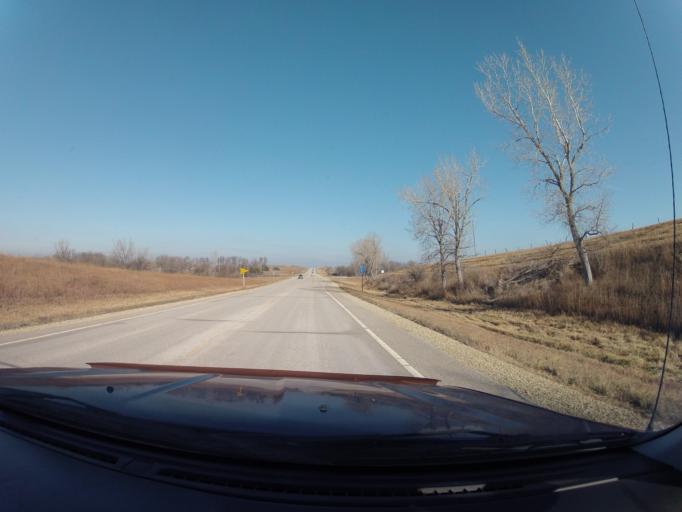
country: US
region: Kansas
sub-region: Marshall County
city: Blue Rapids
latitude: 39.5353
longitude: -96.7552
